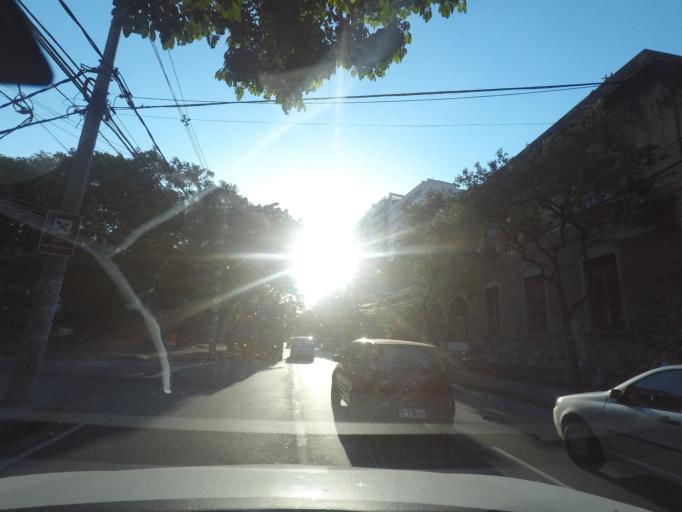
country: BR
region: Rio de Janeiro
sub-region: Rio De Janeiro
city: Rio de Janeiro
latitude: -22.9172
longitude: -43.2145
